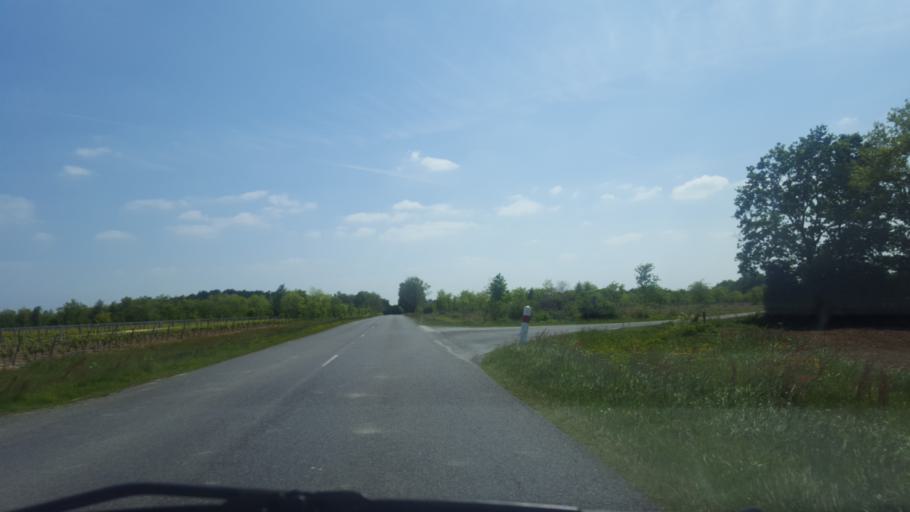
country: FR
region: Pays de la Loire
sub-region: Departement de la Loire-Atlantique
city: La Limouziniere
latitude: 46.9831
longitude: -1.5689
